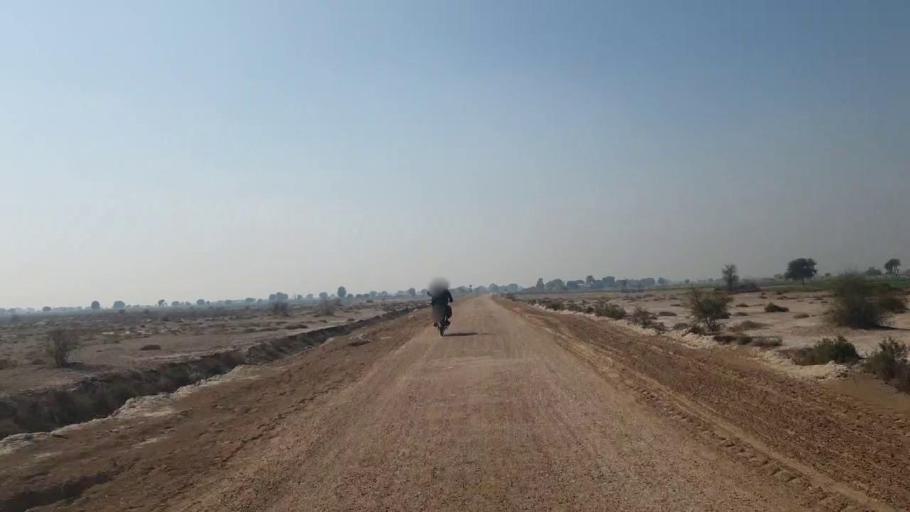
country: PK
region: Sindh
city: Shahpur Chakar
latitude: 26.1131
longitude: 68.6089
